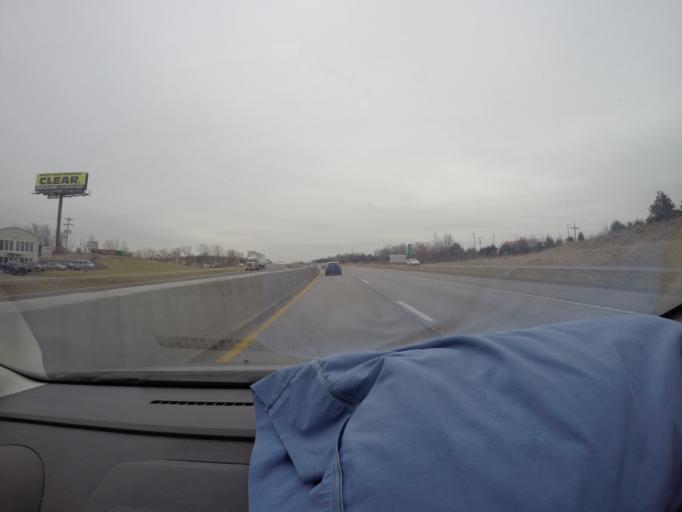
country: US
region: Missouri
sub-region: Warren County
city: Wright City
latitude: 38.8275
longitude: -91.0090
